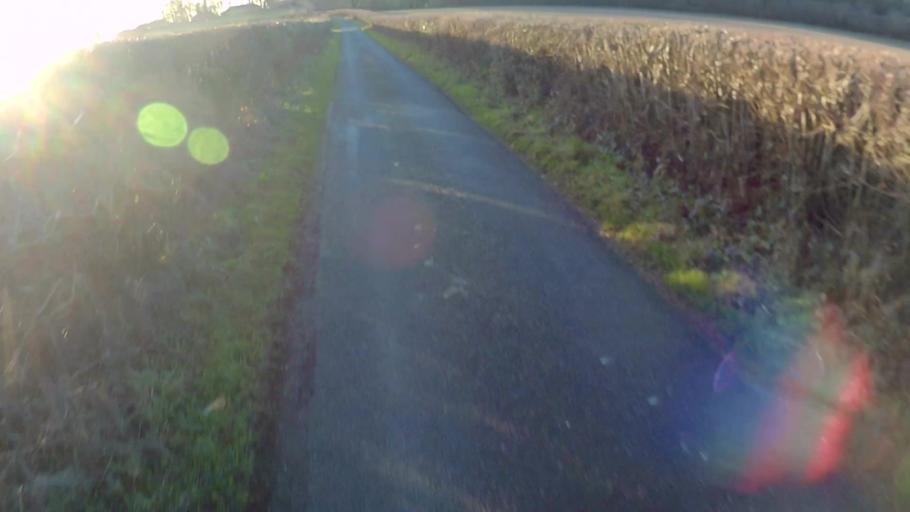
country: GB
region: England
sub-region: Hampshire
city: Basingstoke
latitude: 51.2131
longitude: -1.1395
